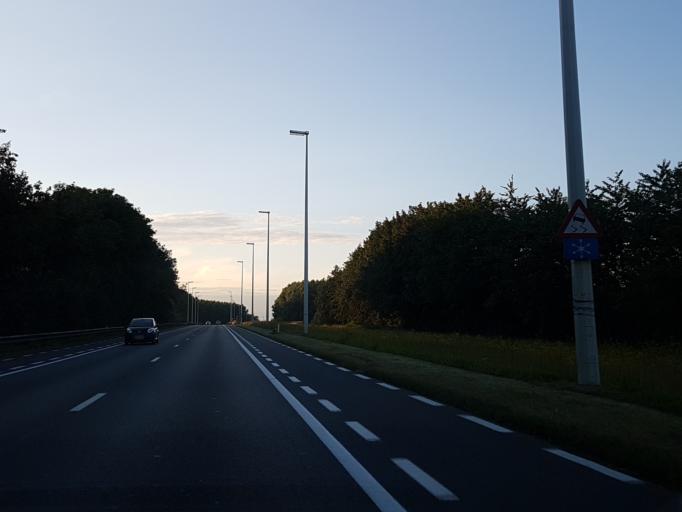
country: BE
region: Flanders
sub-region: Provincie Oost-Vlaanderen
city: Hamme
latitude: 51.1039
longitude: 4.1454
